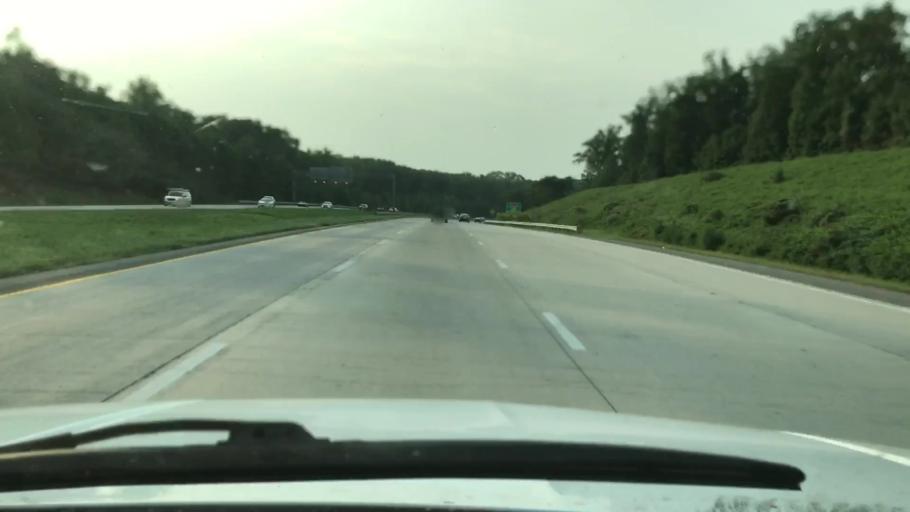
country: US
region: Virginia
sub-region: Chesterfield County
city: Brandermill
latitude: 37.4743
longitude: -77.6568
